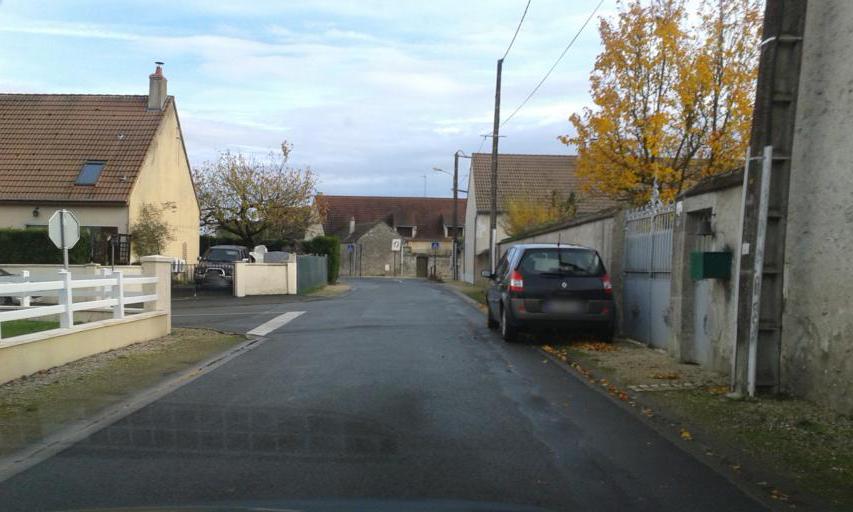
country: FR
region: Centre
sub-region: Departement du Loiret
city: Beaugency
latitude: 47.8108
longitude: 1.6373
